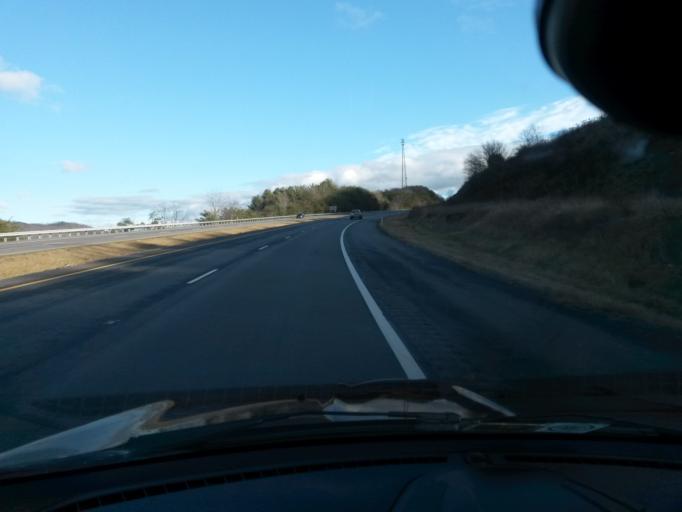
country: US
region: West Virginia
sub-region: Mercer County
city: Athens
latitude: 37.3435
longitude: -80.9839
